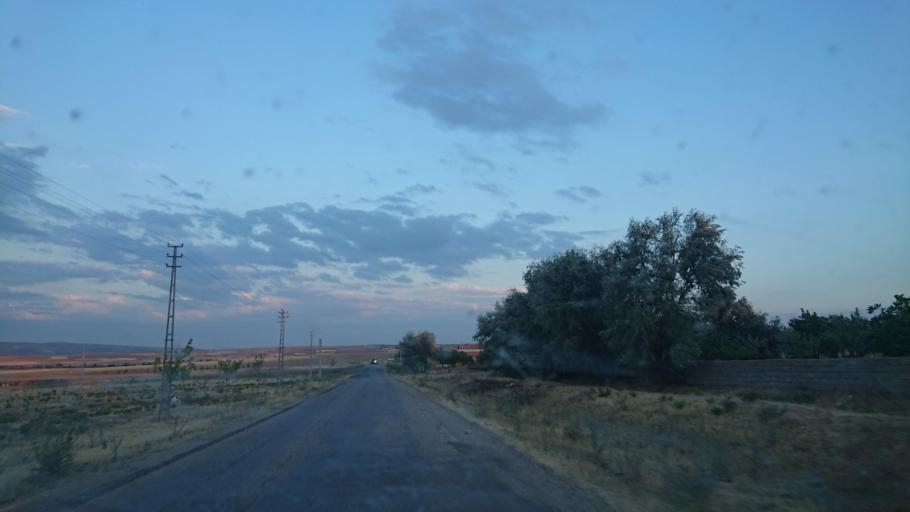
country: TR
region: Aksaray
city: Balci
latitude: 38.8274
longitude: 34.0969
